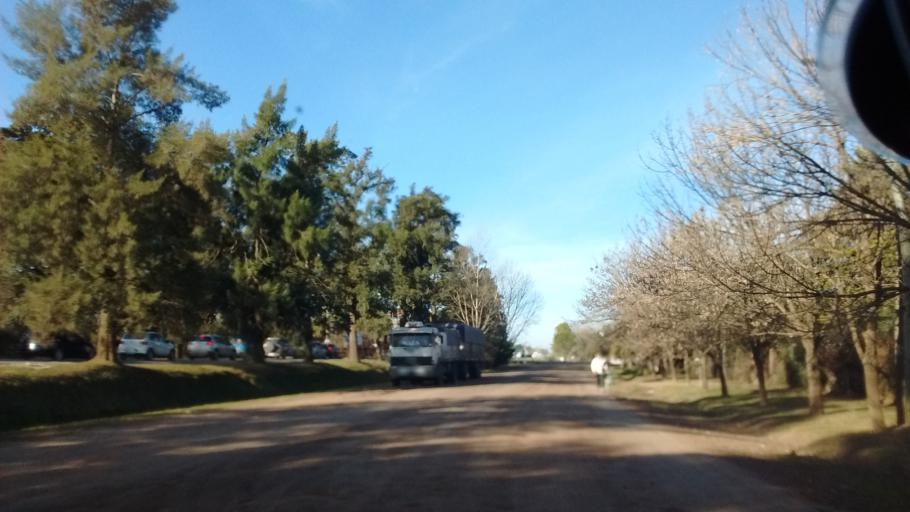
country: AR
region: Santa Fe
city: Funes
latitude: -32.9231
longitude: -60.8018
